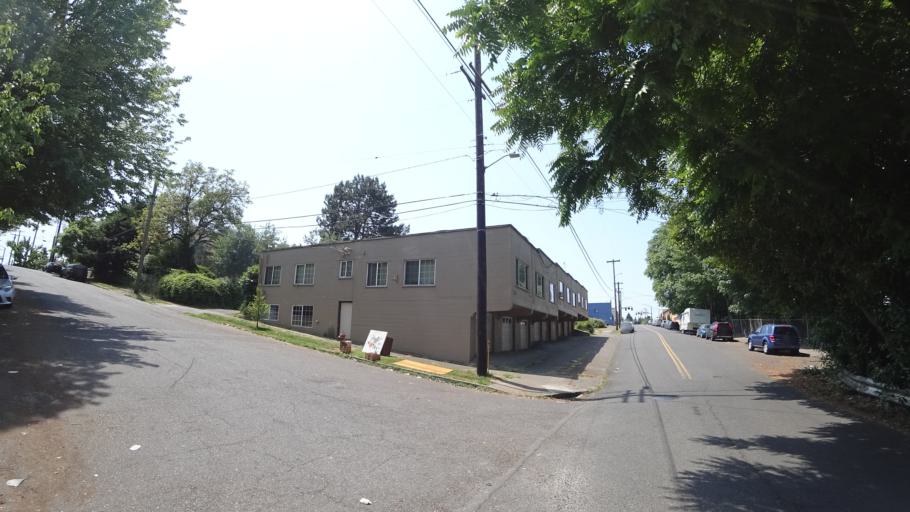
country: US
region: Washington
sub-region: Clark County
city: Vancouver
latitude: 45.5845
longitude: -122.6846
